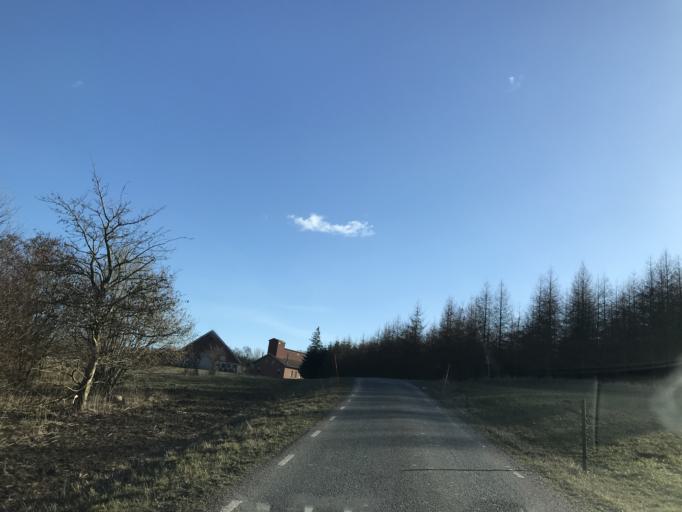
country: SE
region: Skane
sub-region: Ystads Kommun
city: Ystad
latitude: 55.5538
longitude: 13.8075
